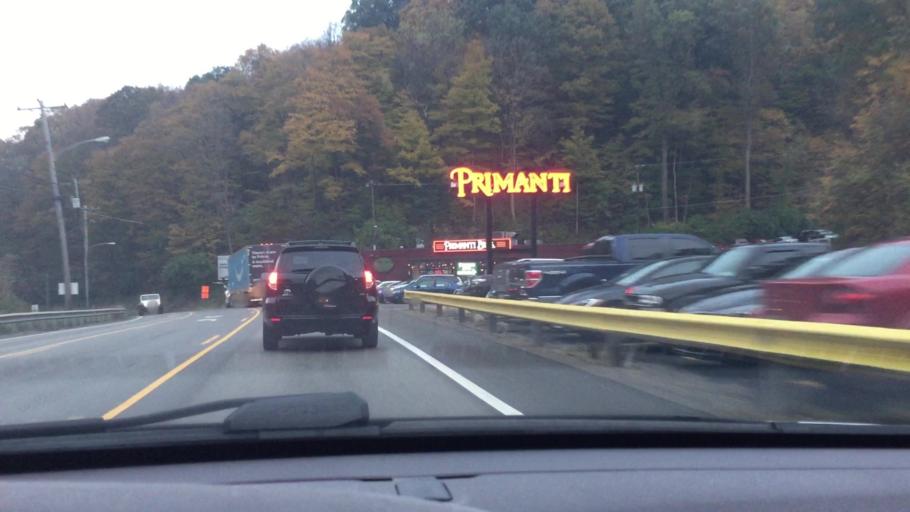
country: US
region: Pennsylvania
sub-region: Allegheny County
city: Ingram
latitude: 40.4451
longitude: -80.0997
